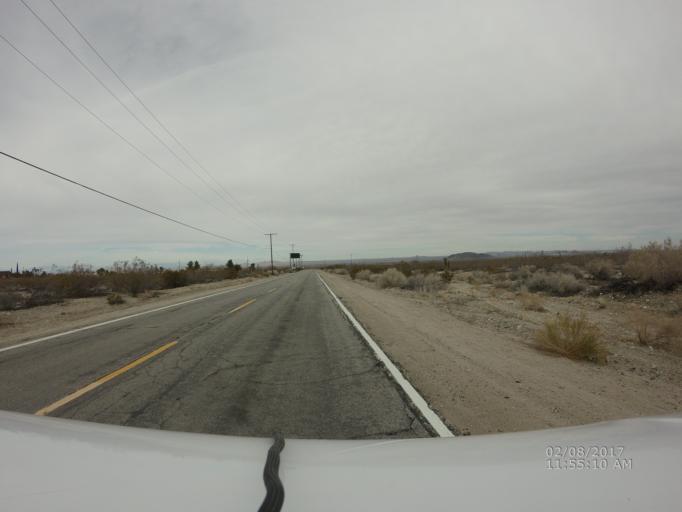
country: US
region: California
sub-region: Los Angeles County
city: Lake Los Angeles
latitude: 34.4962
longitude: -117.7651
